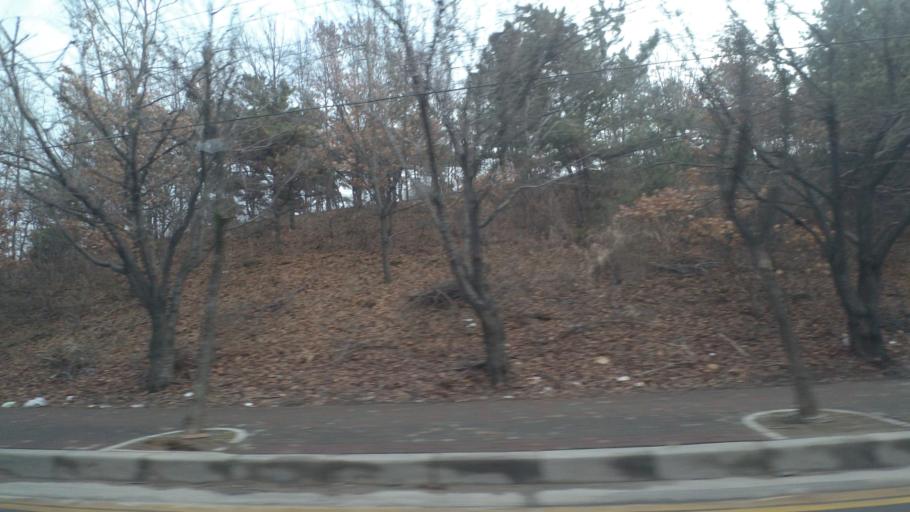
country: KR
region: Gyeonggi-do
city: Hwaseong-si
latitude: 36.9899
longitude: 126.8524
